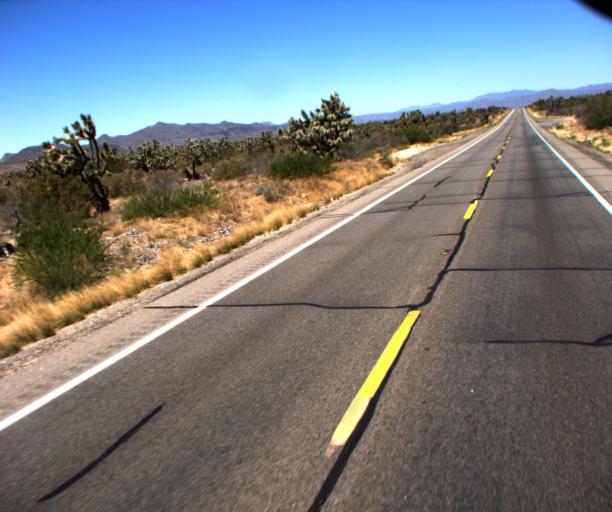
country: US
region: Arizona
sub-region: Yavapai County
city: Congress
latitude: 34.2592
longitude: -113.0872
